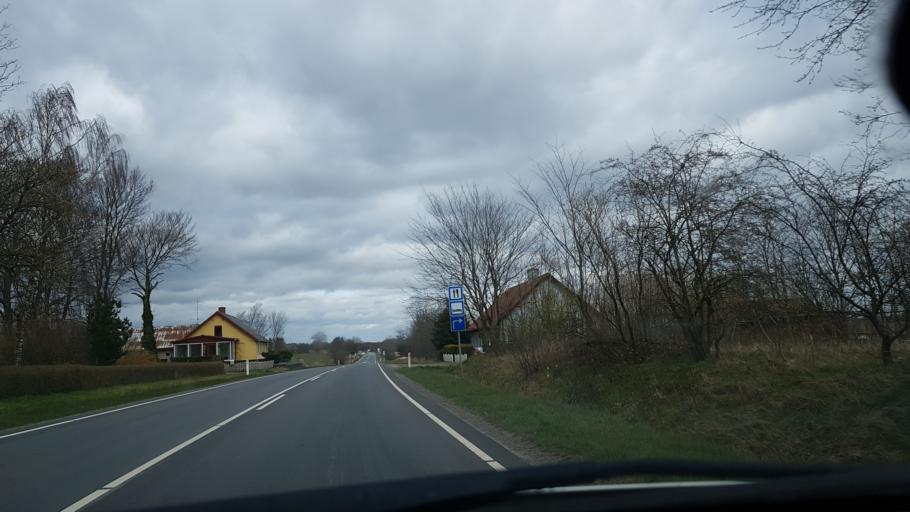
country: DK
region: South Denmark
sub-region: Vejen Kommune
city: Holsted
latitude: 55.4331
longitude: 8.9080
